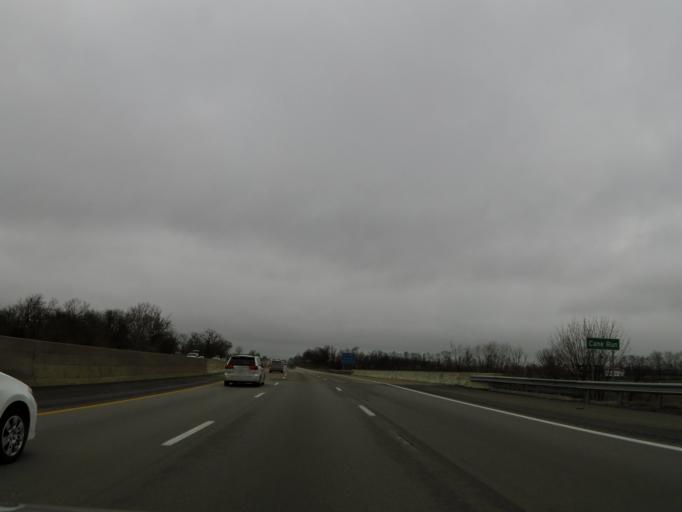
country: US
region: Kentucky
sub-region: Scott County
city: Georgetown
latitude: 38.1661
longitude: -84.5367
